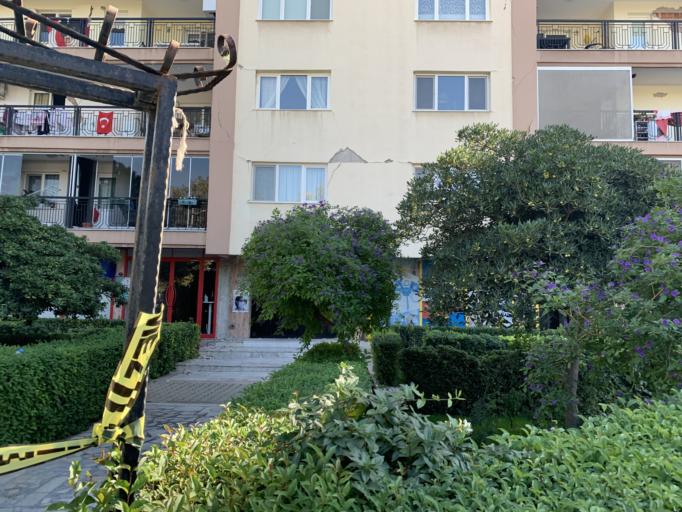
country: TR
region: Izmir
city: Bornova
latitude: 38.4553
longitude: 27.1909
